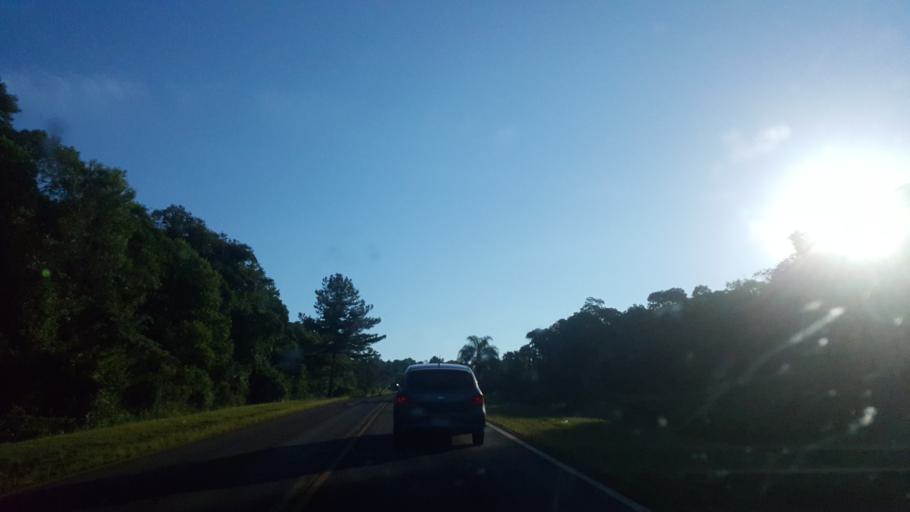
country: AR
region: Misiones
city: El Alcazar
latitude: -26.7208
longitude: -54.8599
